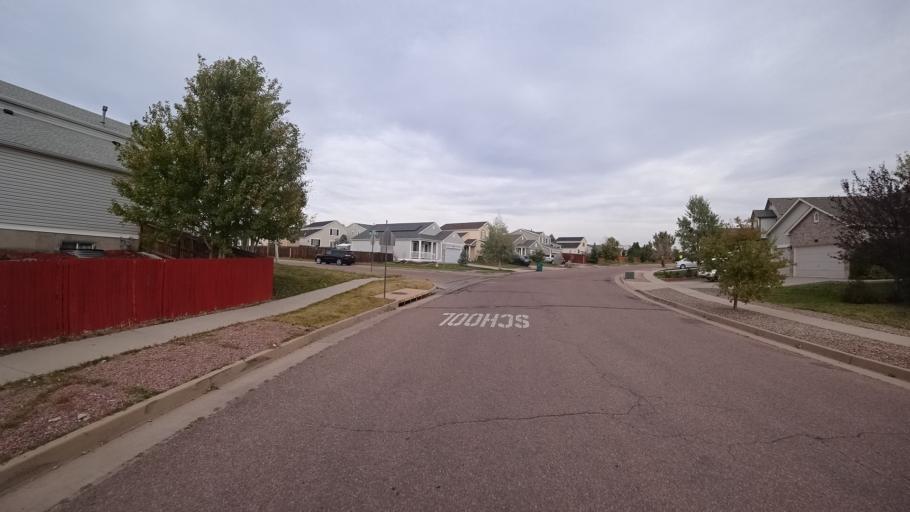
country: US
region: Colorado
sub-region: El Paso County
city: Cimarron Hills
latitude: 38.9181
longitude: -104.7111
